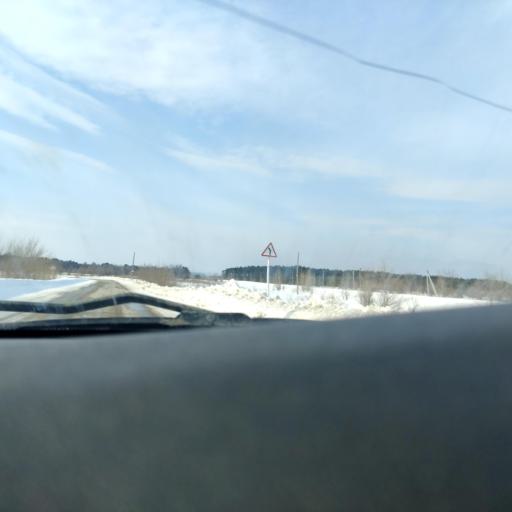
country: RU
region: Samara
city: Rozhdestveno
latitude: 53.2405
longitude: 50.0415
